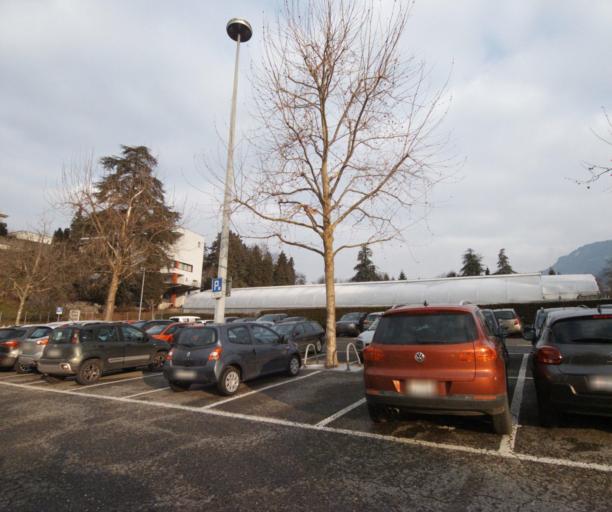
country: CH
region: Vaud
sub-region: Riviera-Pays-d'Enhaut District
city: Le Chatelard
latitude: 46.4463
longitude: 6.8788
